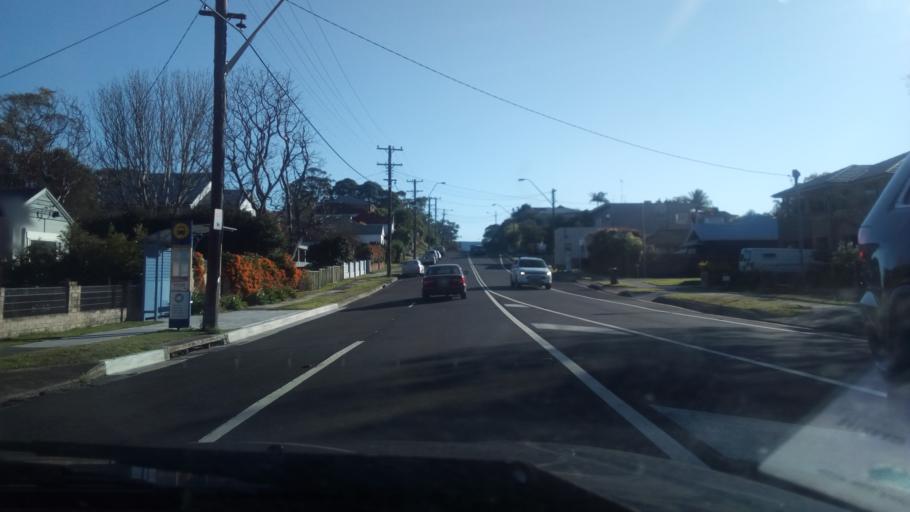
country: AU
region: New South Wales
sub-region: Wollongong
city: Corrimal
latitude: -34.3659
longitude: 150.8984
